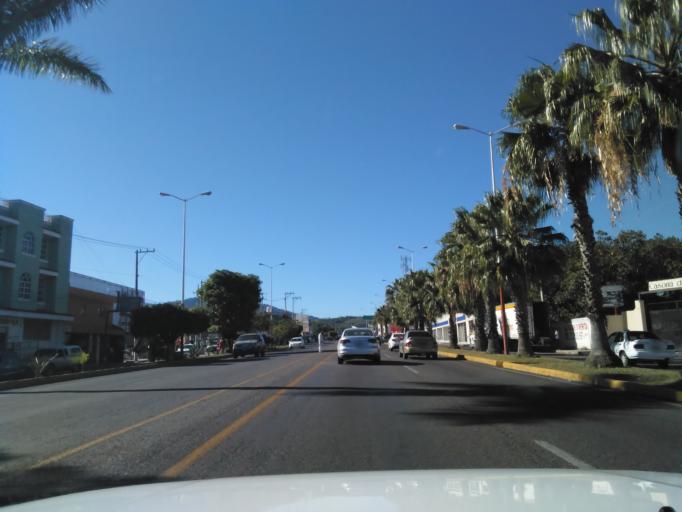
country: MX
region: Nayarit
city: Xalisco
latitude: 21.4530
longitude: -104.8978
